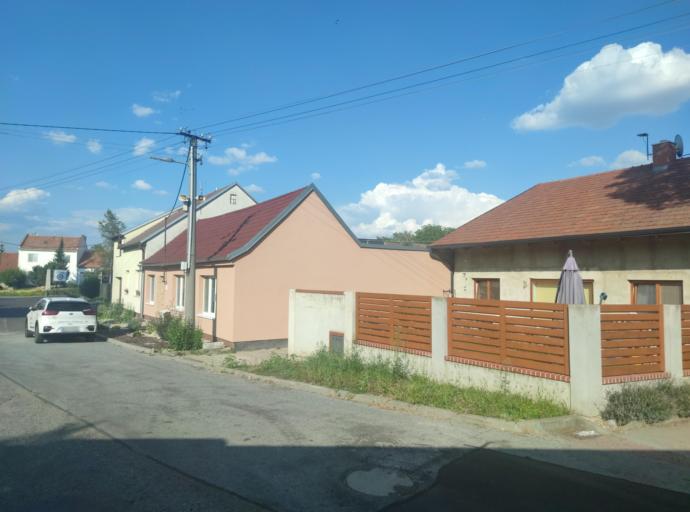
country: CZ
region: South Moravian
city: Slavkov u Brna
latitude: 49.1805
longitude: 16.8487
